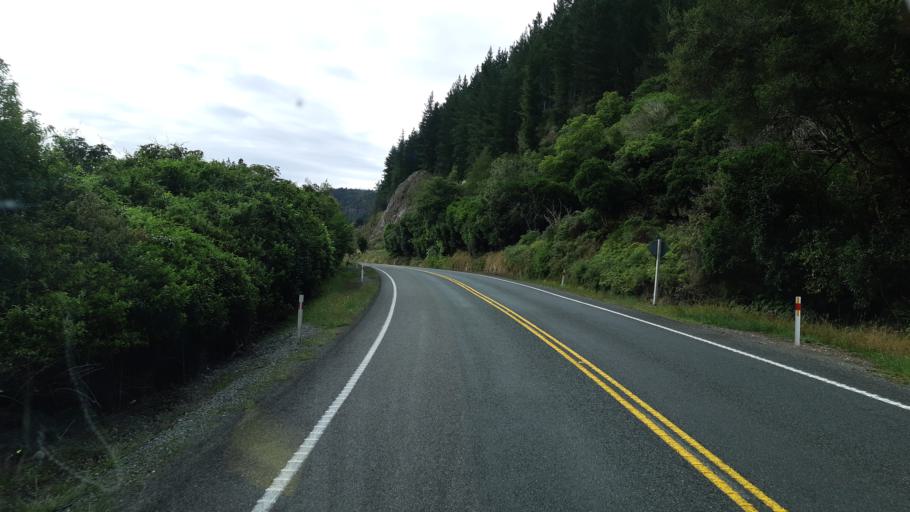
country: NZ
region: West Coast
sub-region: Buller District
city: Westport
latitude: -41.7786
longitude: 172.2476
